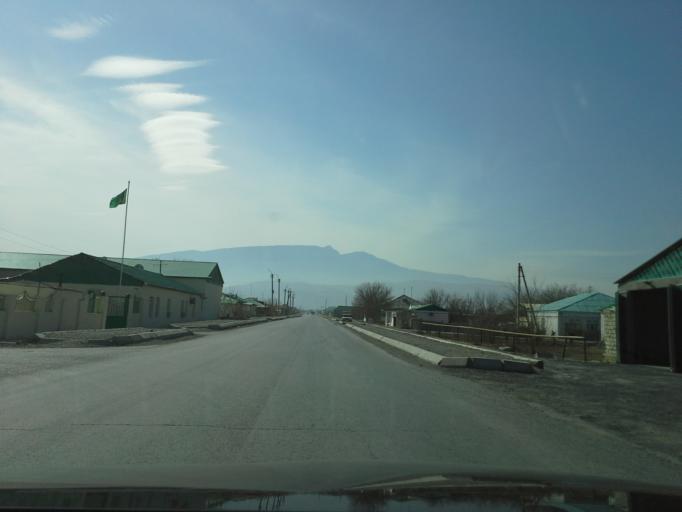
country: TM
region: Ahal
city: Abadan
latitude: 38.1126
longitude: 58.0348
